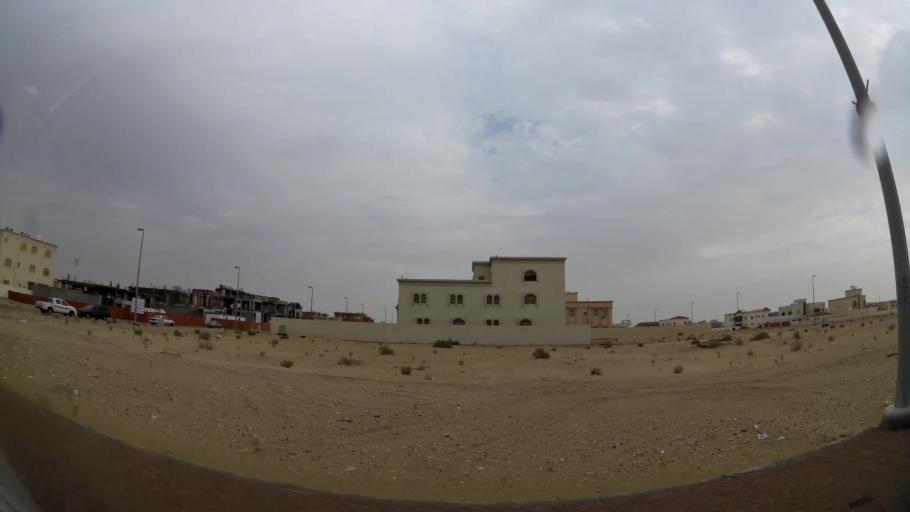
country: AE
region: Abu Dhabi
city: Abu Dhabi
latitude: 24.3638
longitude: 54.6207
